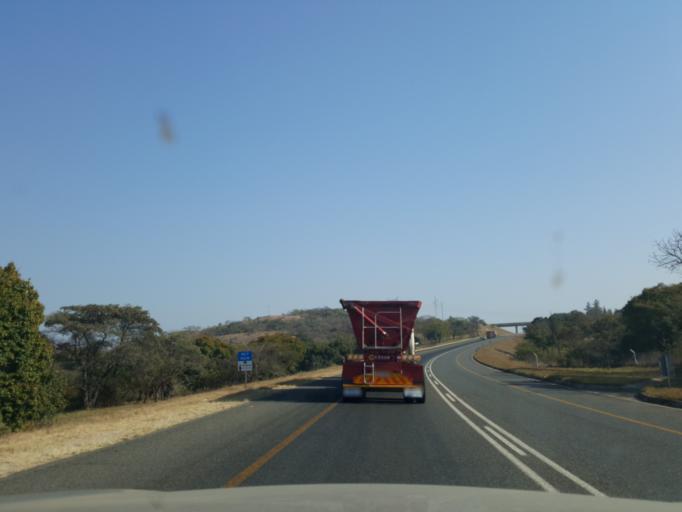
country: ZA
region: Mpumalanga
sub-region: Ehlanzeni District
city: Nelspruit
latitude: -25.4450
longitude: 30.9846
